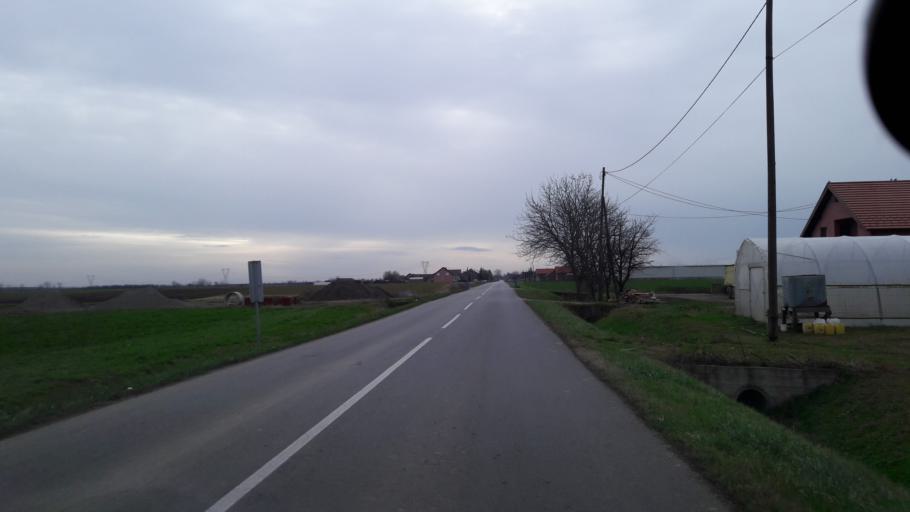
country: HR
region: Osjecko-Baranjska
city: Vladislavci
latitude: 45.4755
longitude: 18.5603
